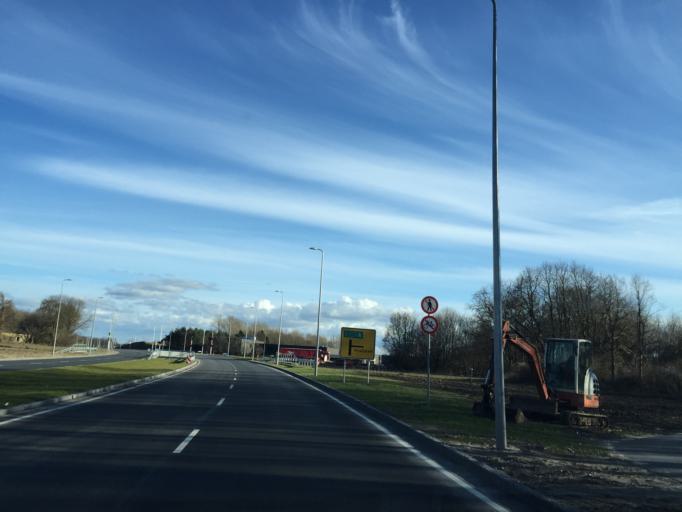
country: DK
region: South Denmark
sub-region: Odense Kommune
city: Hojby
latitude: 55.3585
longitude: 10.4149
